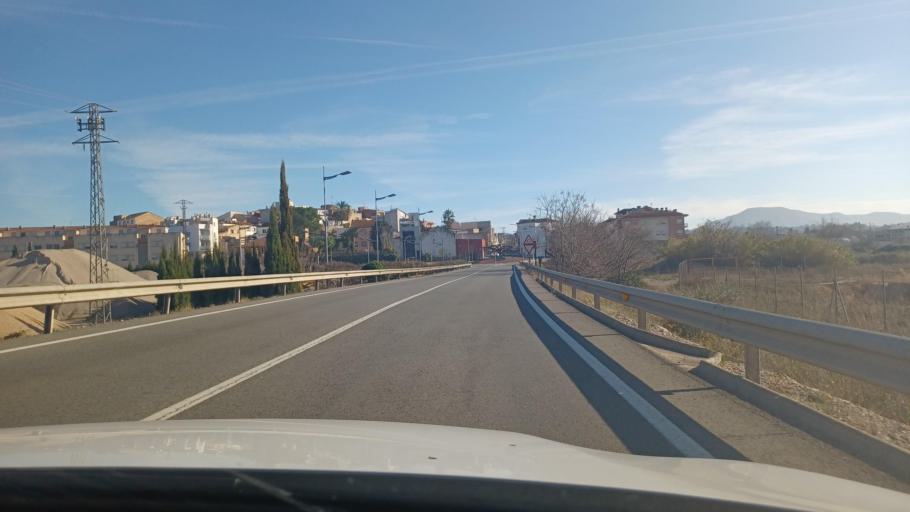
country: ES
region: Catalonia
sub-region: Provincia de Tarragona
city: Masdenverge
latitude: 40.7163
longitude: 0.5273
